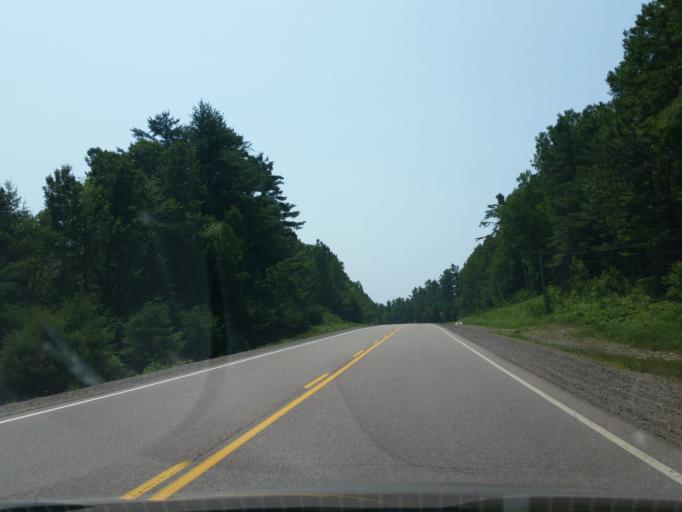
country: CA
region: Ontario
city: Deep River
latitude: 46.1955
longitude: -77.8798
